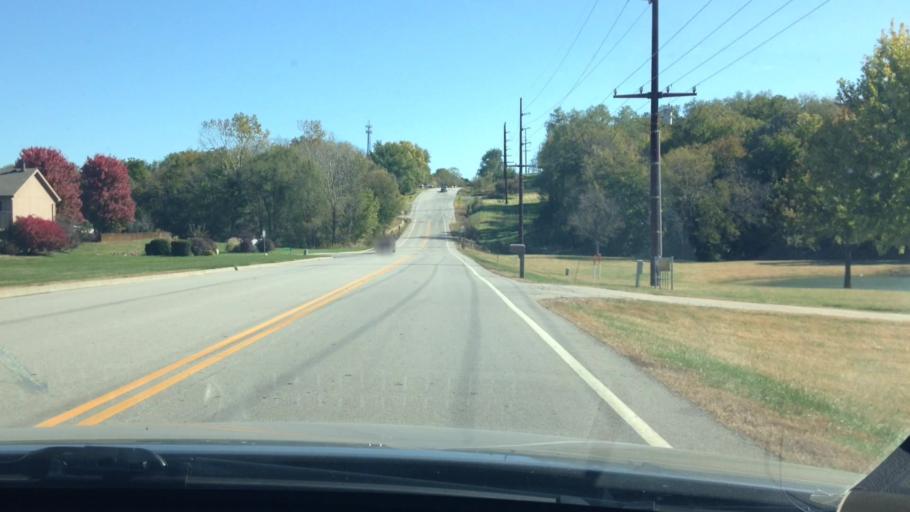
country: US
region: Missouri
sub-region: Platte County
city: Platte City
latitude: 39.3395
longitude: -94.7597
